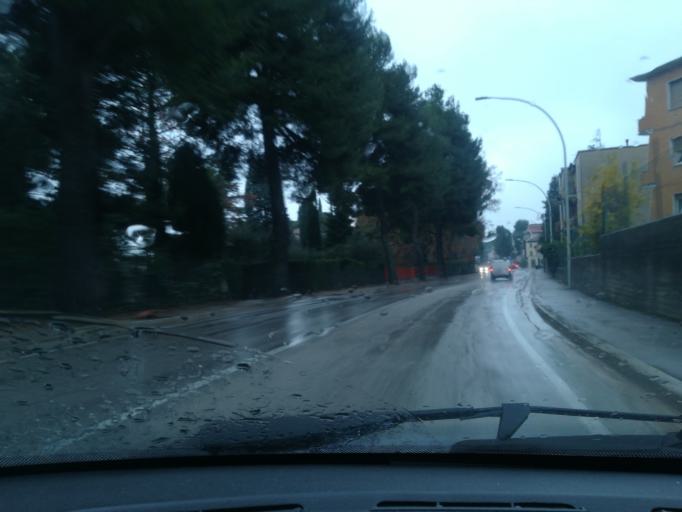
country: IT
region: The Marches
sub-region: Provincia di Macerata
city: Macerata
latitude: 43.2919
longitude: 13.4371
